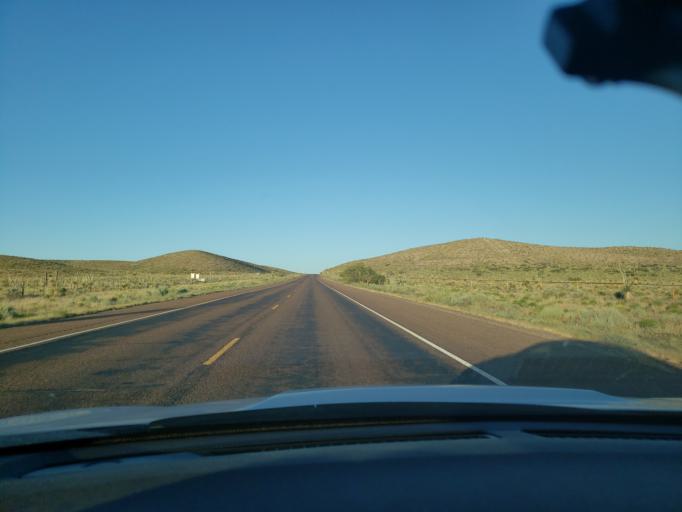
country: US
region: Texas
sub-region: El Paso County
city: Homestead Meadows South
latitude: 31.8268
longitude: -105.9001
